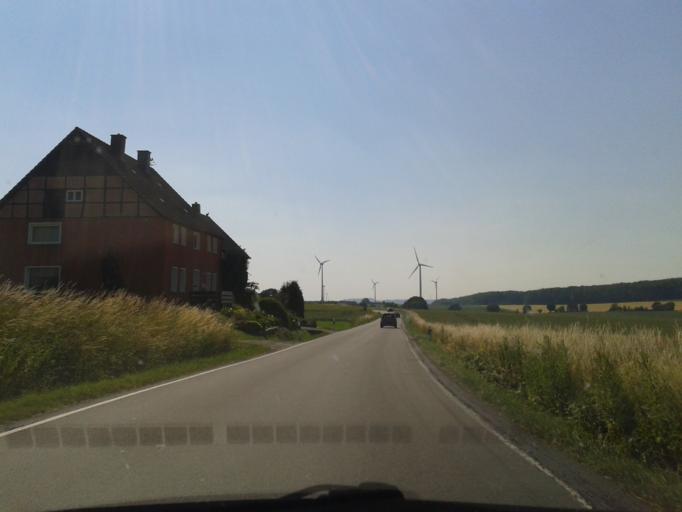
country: DE
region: North Rhine-Westphalia
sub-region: Regierungsbezirk Detmold
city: Blomberg
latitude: 51.9798
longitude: 9.0673
